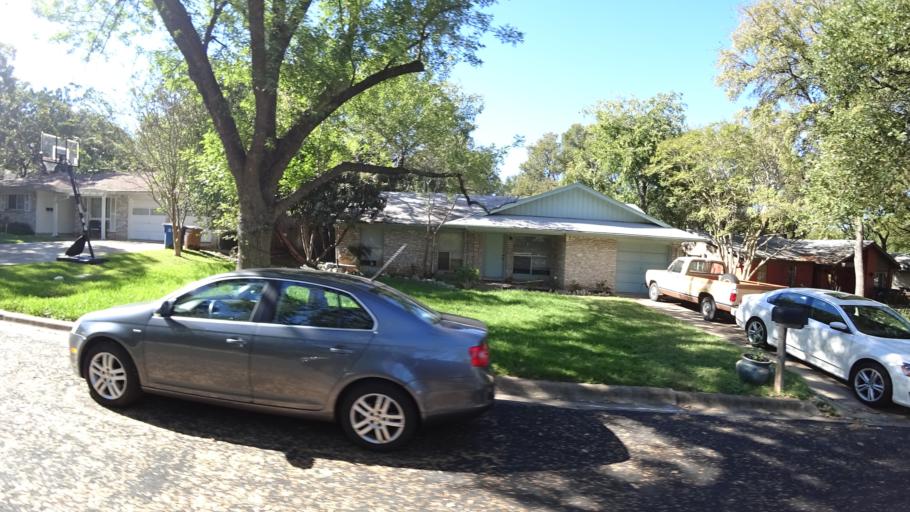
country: US
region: Texas
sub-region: Travis County
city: Rollingwood
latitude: 30.2369
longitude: -97.7807
